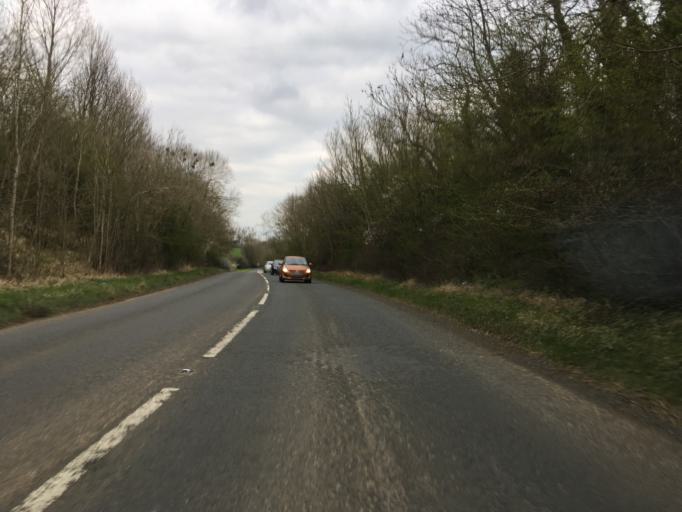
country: GB
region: England
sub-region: Gloucestershire
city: Cirencester
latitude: 51.7310
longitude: -1.9096
